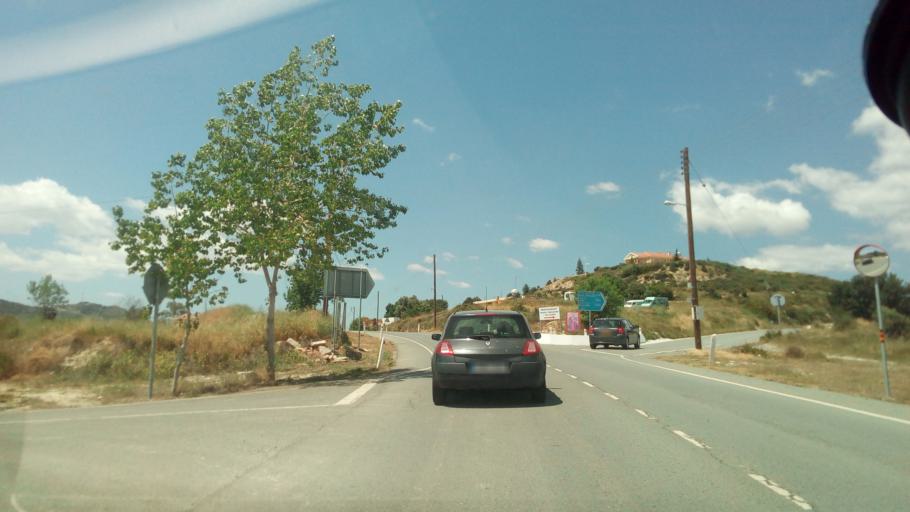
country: CY
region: Limassol
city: Pachna
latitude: 34.7795
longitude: 32.8323
